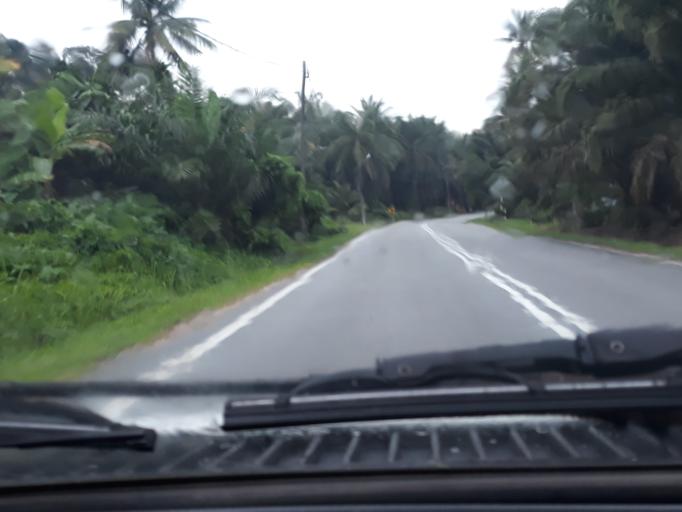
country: MY
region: Kedah
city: Kulim
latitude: 5.2381
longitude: 100.6017
